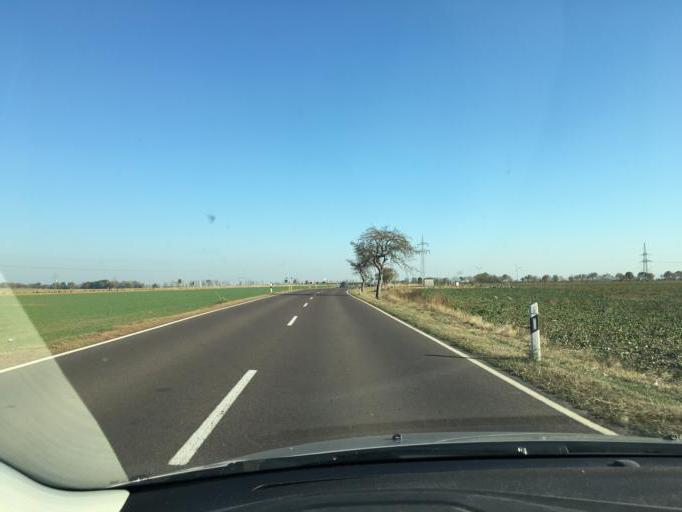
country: DE
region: Saxony-Anhalt
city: Baalberge
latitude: 51.7986
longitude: 11.7864
